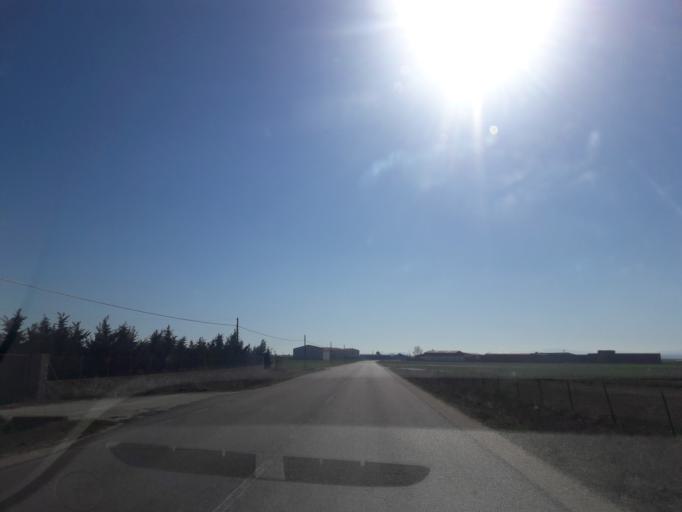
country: ES
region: Castille and Leon
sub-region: Provincia de Salamanca
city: Macotera
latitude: 40.8350
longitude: -5.3009
